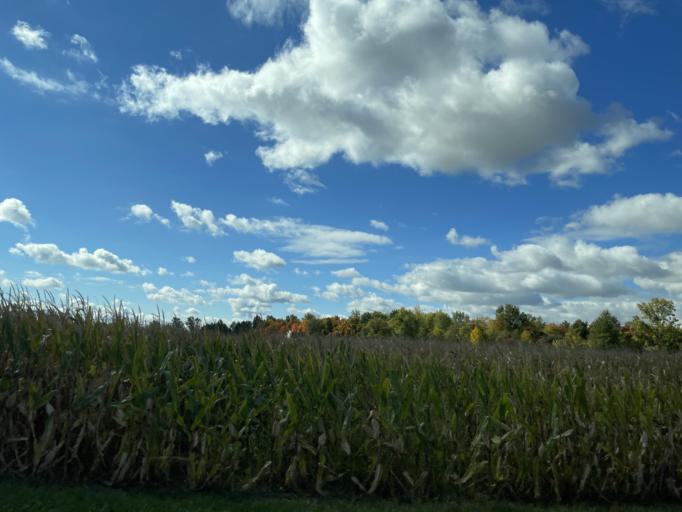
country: US
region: Indiana
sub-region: Allen County
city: Fort Wayne
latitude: 41.1149
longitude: -85.2298
